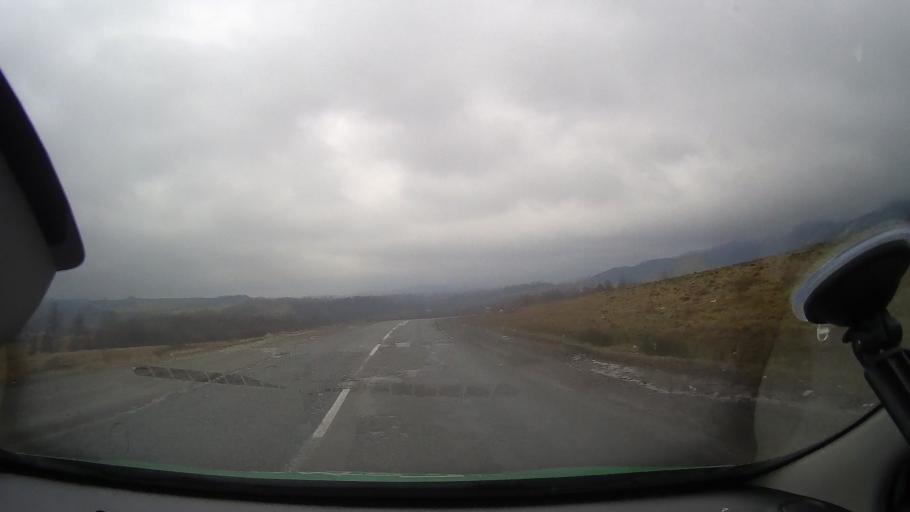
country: RO
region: Arad
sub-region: Comuna Varfurile
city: Varfurile
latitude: 46.2957
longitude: 22.5402
